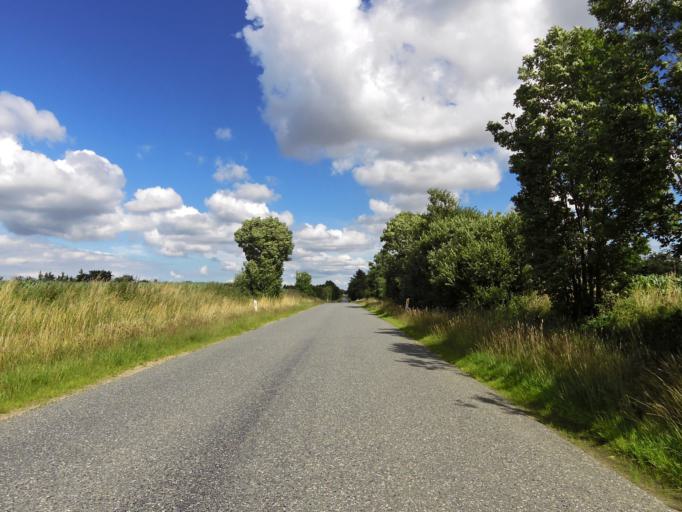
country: DK
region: South Denmark
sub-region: Haderslev Kommune
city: Vojens
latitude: 55.3170
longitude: 9.1919
